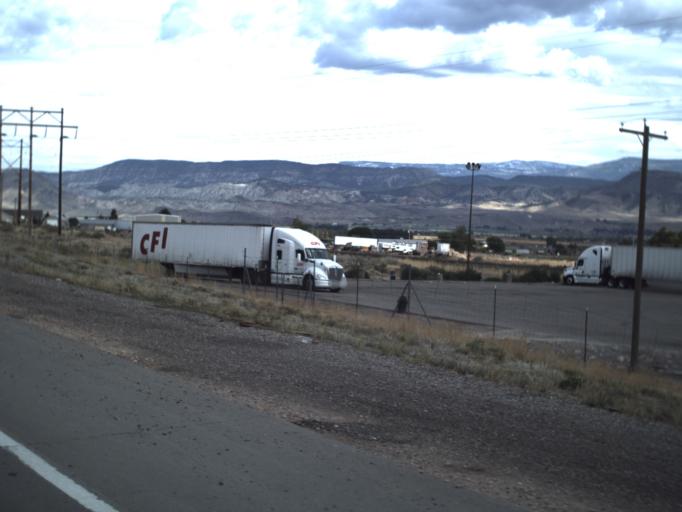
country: US
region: Utah
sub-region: Sevier County
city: Richfield
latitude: 38.7895
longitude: -112.0819
